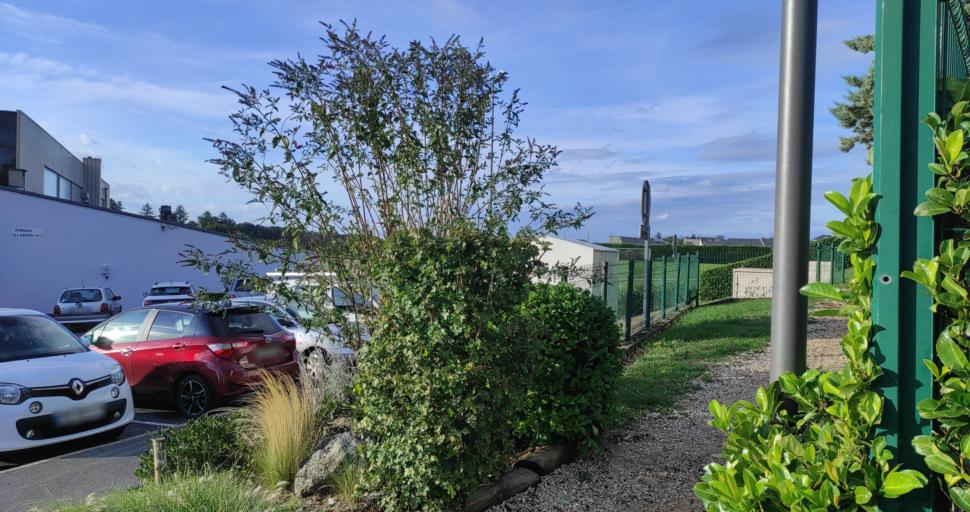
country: FR
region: Midi-Pyrenees
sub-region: Departement de l'Aveyron
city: Rodez
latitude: 44.3775
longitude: 2.5694
